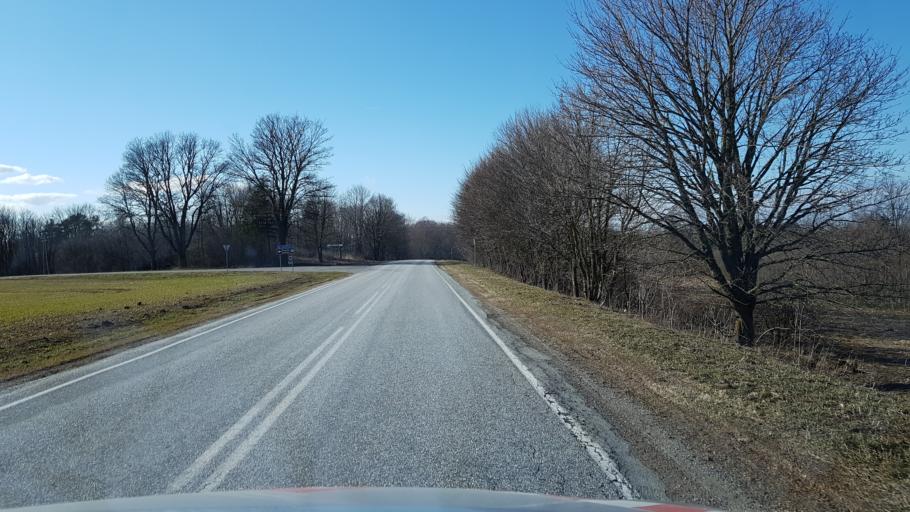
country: EE
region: Laeaene-Virumaa
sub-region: Haljala vald
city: Haljala
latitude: 59.4752
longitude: 26.1641
